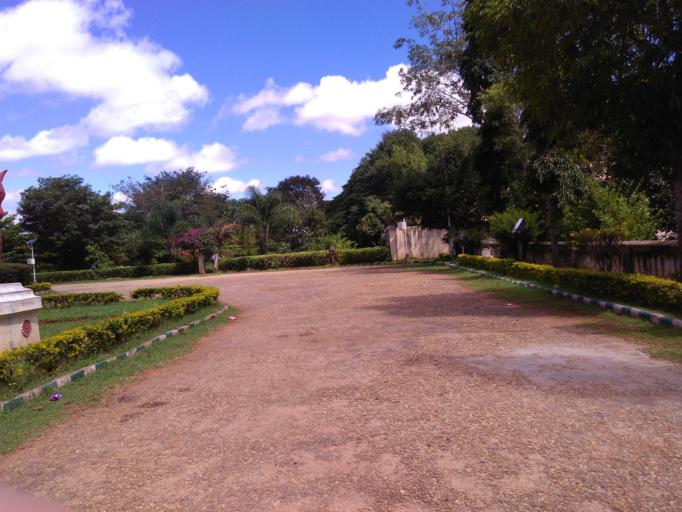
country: IN
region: Karnataka
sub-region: Mysore
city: Mysore
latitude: 12.3138
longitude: 76.6228
